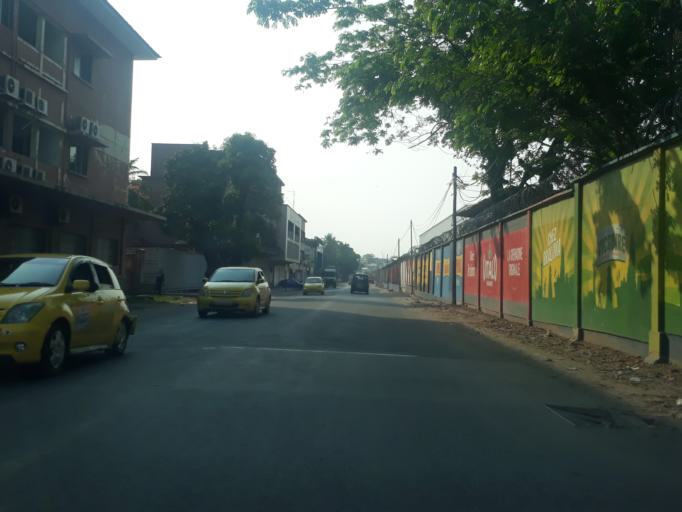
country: CD
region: Kinshasa
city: Kinshasa
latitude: -4.3101
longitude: 15.3285
